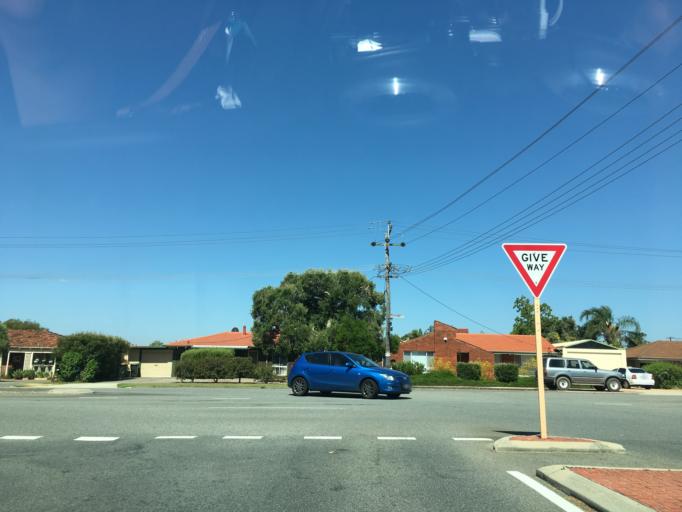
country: AU
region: Western Australia
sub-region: Canning
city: Willetton
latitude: -32.0478
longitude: 115.9038
